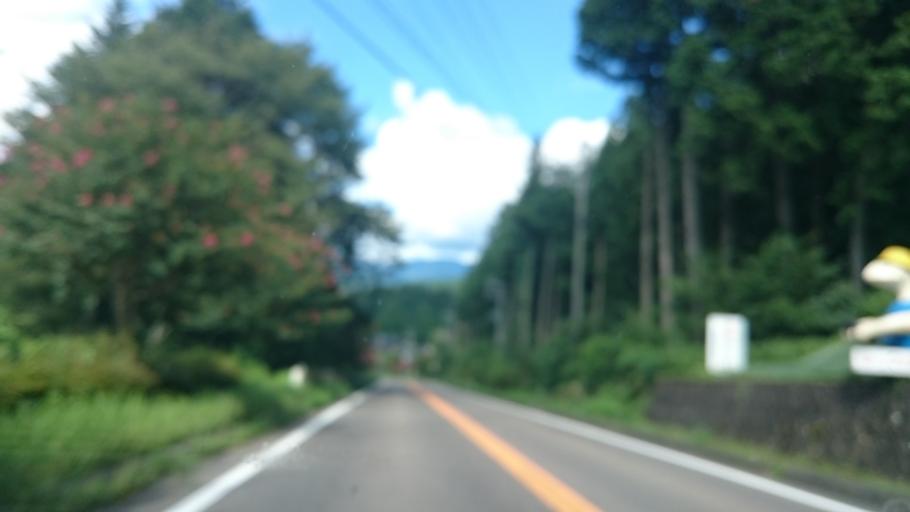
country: JP
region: Gifu
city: Nakatsugawa
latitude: 35.5853
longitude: 137.4605
